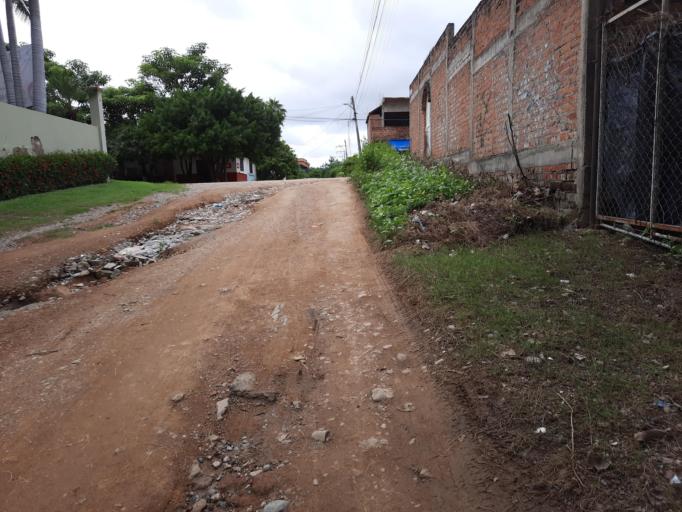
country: MX
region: Jalisco
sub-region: Puerto Vallarta
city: Puerto Vallarta
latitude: 20.6588
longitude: -105.2104
